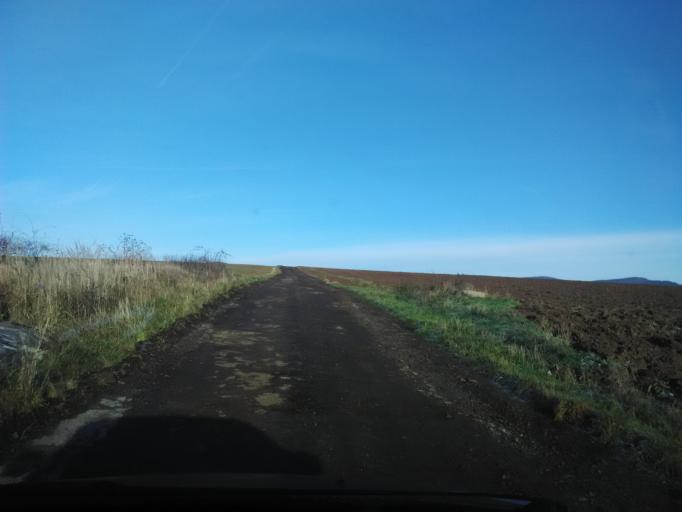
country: SK
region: Nitriansky
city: Tlmace
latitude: 48.3381
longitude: 18.5294
